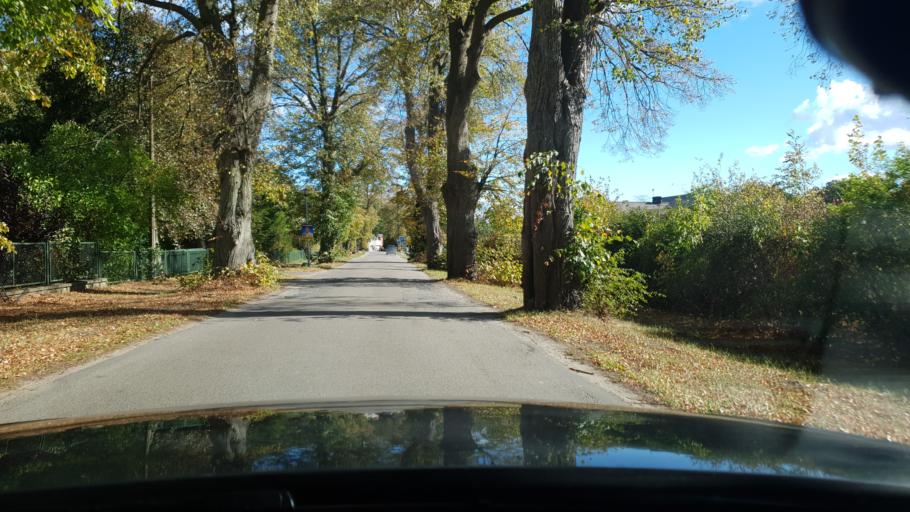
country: PL
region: Pomeranian Voivodeship
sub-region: Powiat pucki
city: Zelistrzewo
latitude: 54.6862
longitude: 18.4600
